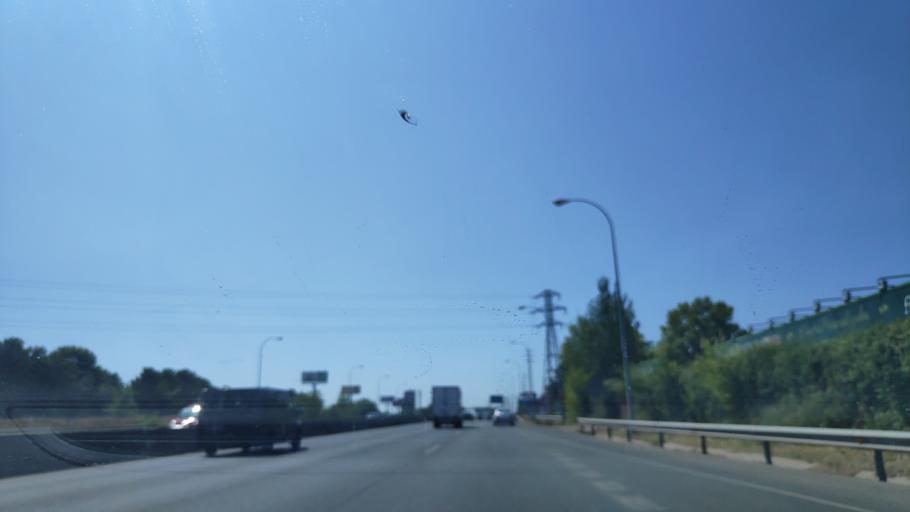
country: ES
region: Madrid
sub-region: Provincia de Madrid
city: Villaverde
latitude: 40.3486
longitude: -3.7230
